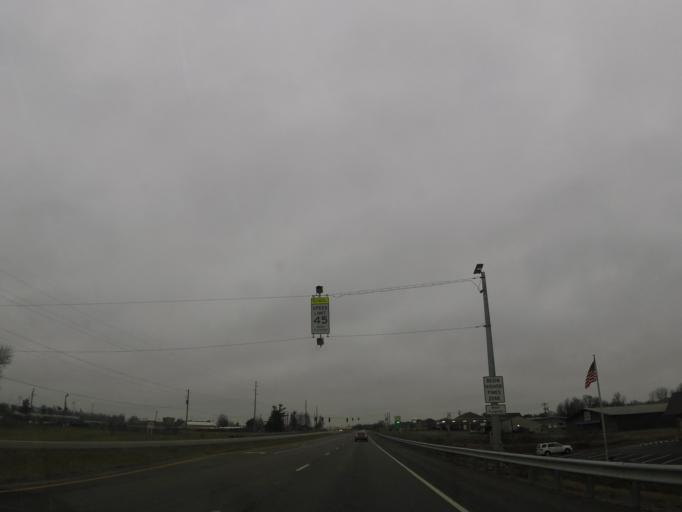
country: US
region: Kentucky
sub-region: Boyle County
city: Danville
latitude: 37.6570
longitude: -84.7973
